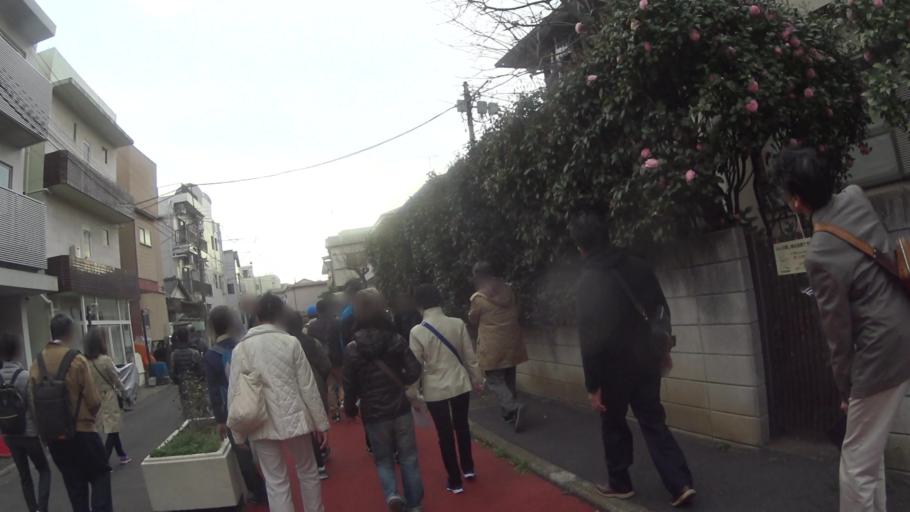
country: JP
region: Tokyo
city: Tokyo
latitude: 35.6876
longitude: 139.6810
